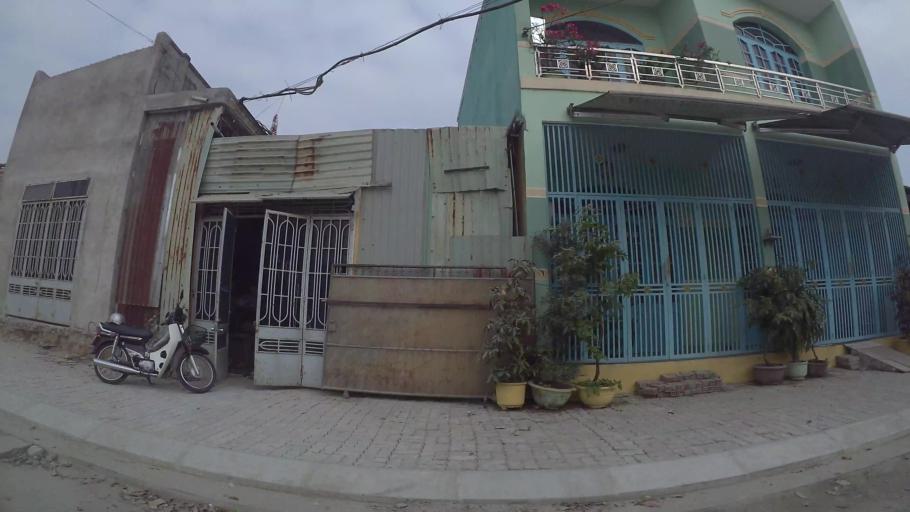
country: VN
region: Da Nang
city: Son Tra
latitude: 16.0649
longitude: 108.2397
